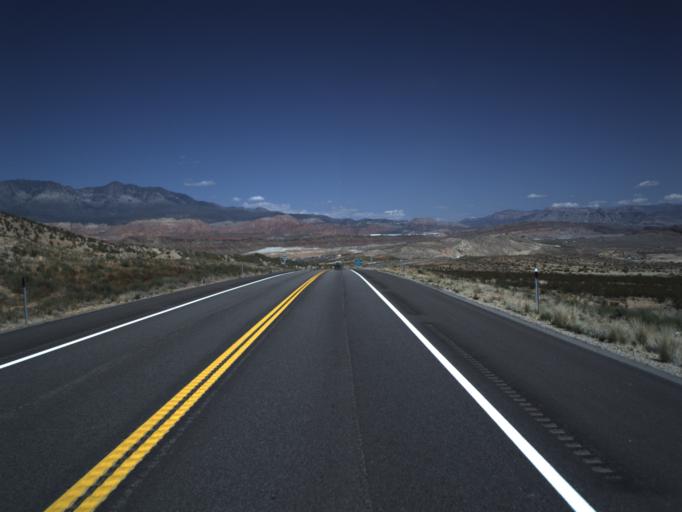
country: US
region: Utah
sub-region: Washington County
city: Washington
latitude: 37.1029
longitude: -113.4654
